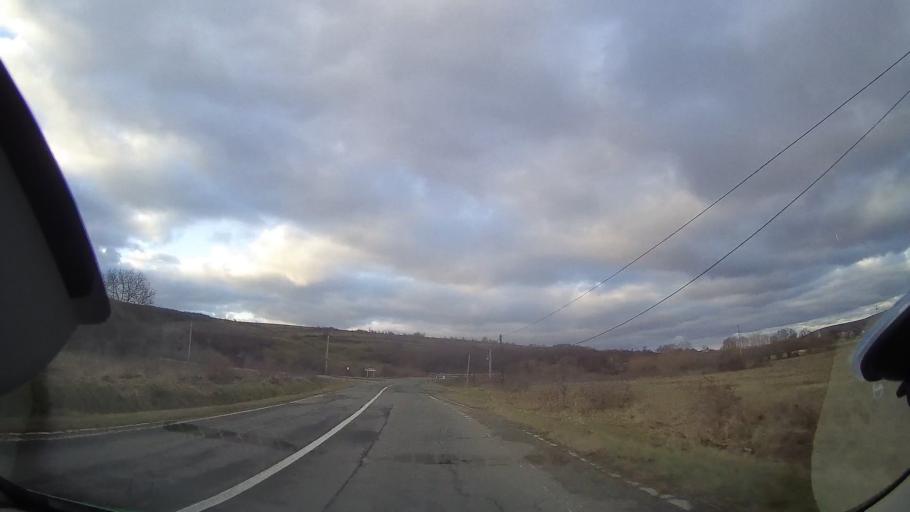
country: RO
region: Cluj
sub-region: Comuna Calatele
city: Calatele
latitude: 46.7946
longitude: 22.9958
